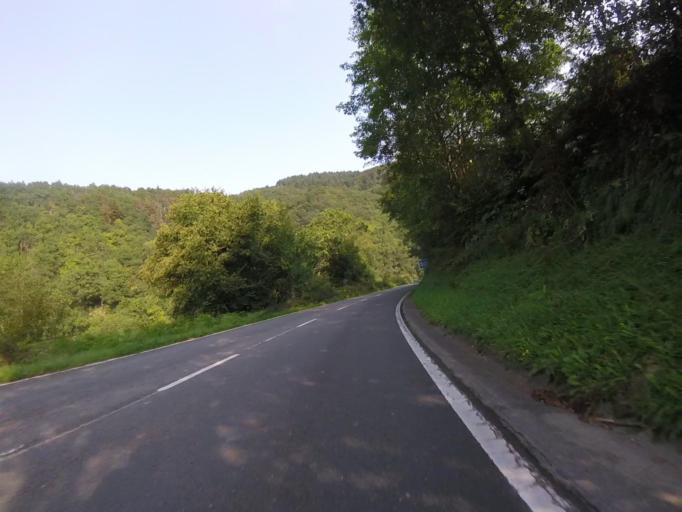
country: ES
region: Navarre
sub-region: Provincia de Navarra
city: Arano
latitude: 43.2195
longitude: -1.9058
